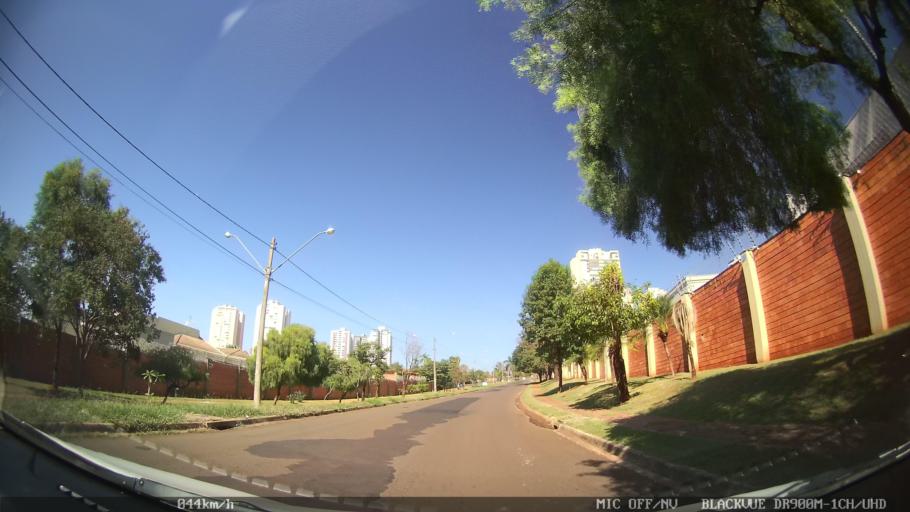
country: BR
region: Sao Paulo
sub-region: Ribeirao Preto
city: Ribeirao Preto
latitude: -21.2131
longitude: -47.8014
